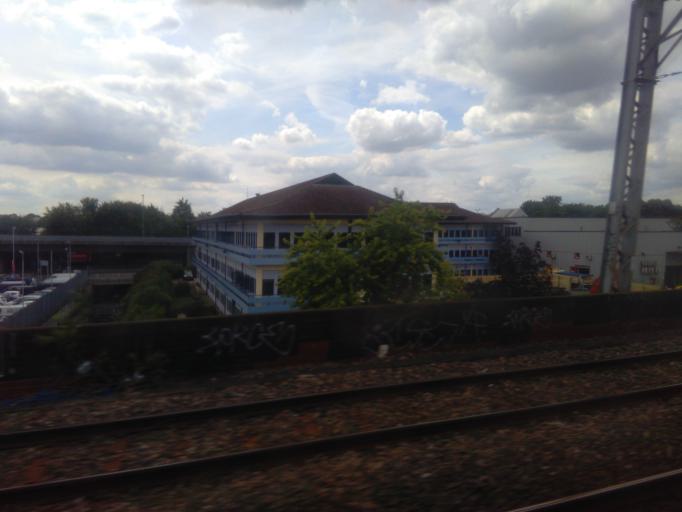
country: GB
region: England
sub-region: Greater London
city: Hendon
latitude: 51.5725
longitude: -0.2317
